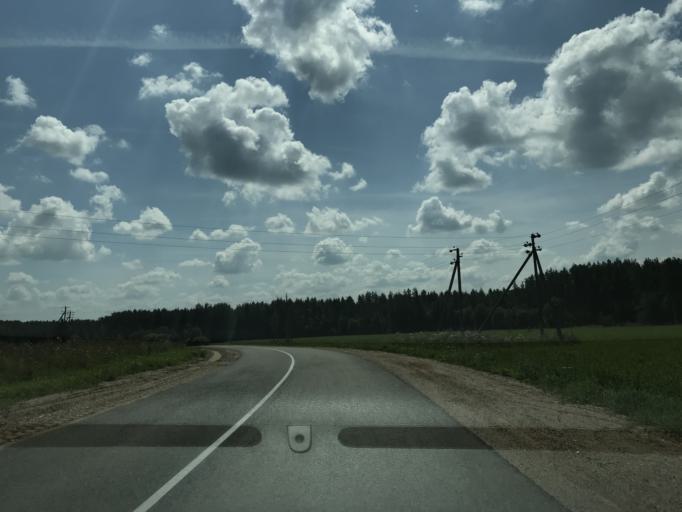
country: BY
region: Minsk
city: Rakaw
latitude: 54.0088
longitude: 26.9810
